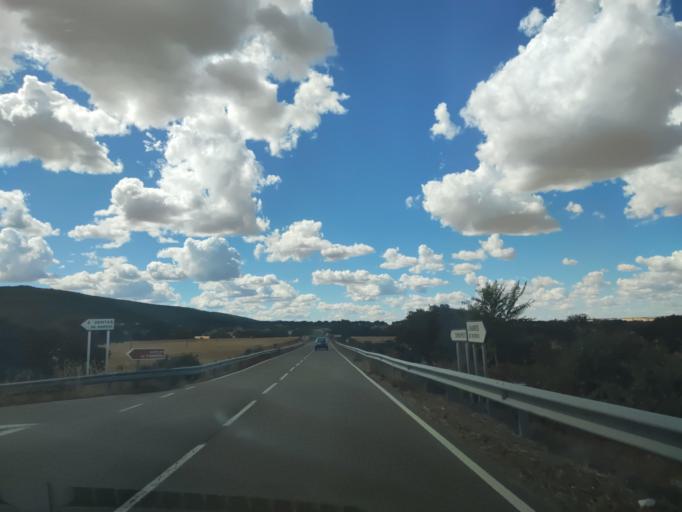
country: ES
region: Castille and Leon
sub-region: Provincia de Salamanca
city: Tejeda y Segoyuela
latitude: 40.6415
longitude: -6.0592
